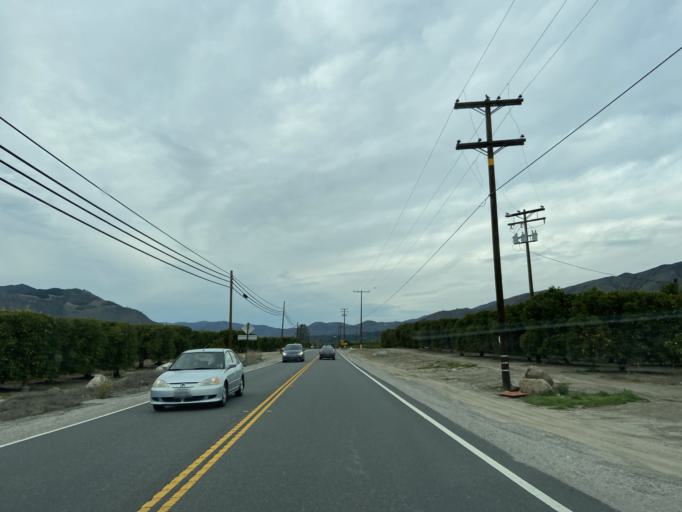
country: US
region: California
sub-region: San Diego County
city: Valley Center
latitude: 33.3162
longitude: -116.9909
